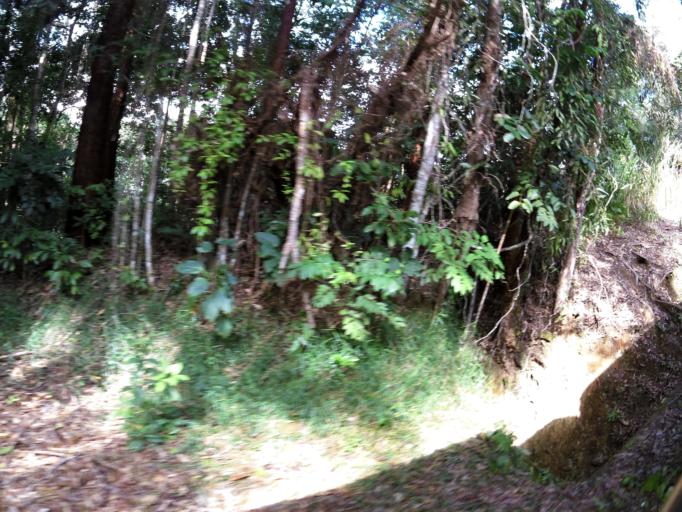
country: AU
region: Queensland
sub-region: Tablelands
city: Kuranda
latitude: -16.8281
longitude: 145.6383
